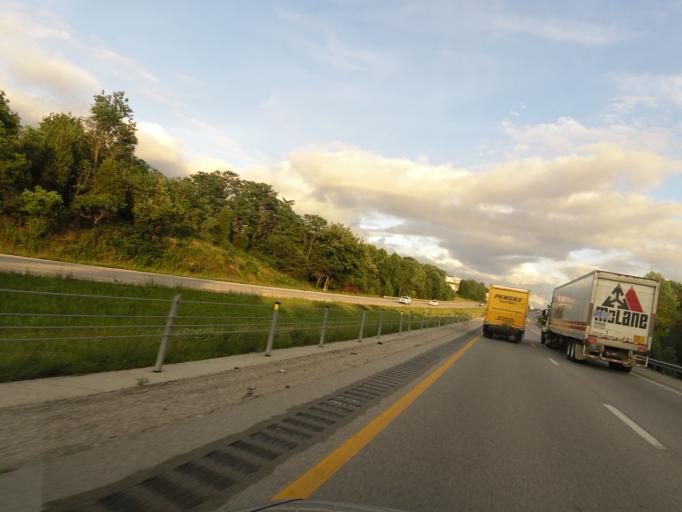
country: US
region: Kentucky
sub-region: Laurel County
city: London
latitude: 37.1820
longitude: -84.1362
